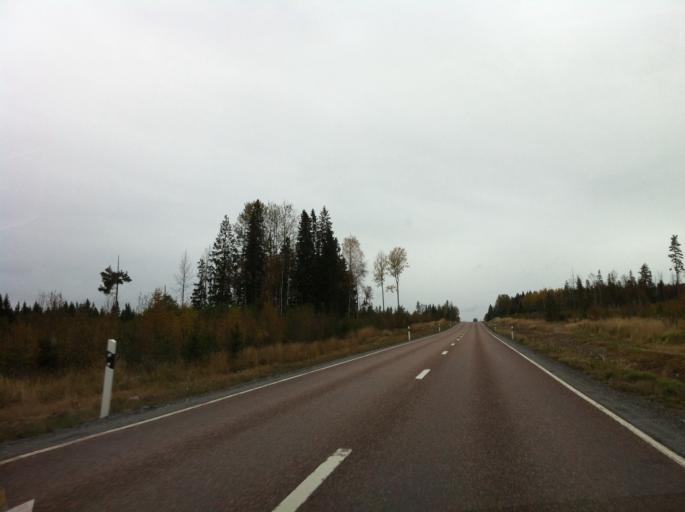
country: SE
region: Dalarna
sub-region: Ludvika Kommun
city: Grangesberg
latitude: 60.0098
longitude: 14.9916
